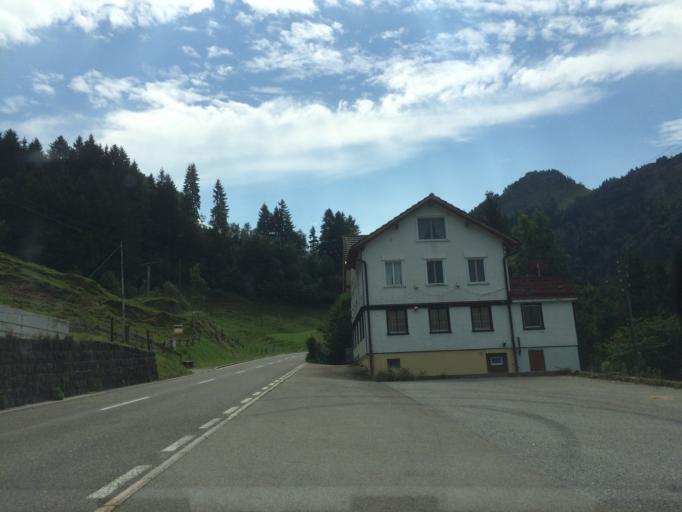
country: CH
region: Appenzell Ausserrhoden
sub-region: Bezirk Hinterland
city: Urnasch
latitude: 47.2860
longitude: 9.2797
